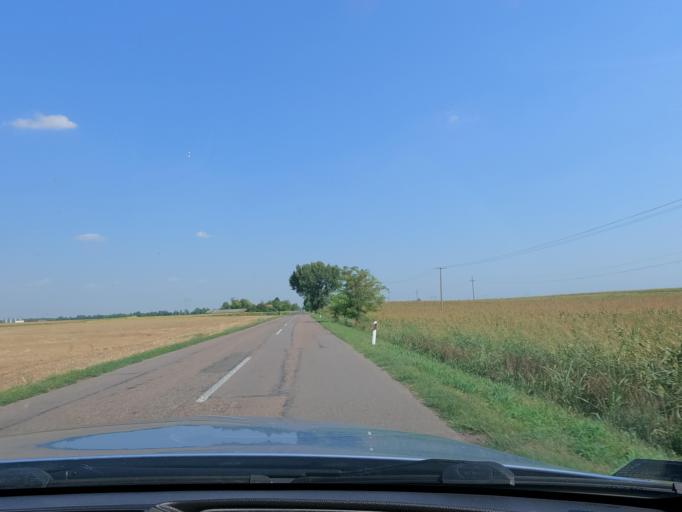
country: RS
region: Autonomna Pokrajina Vojvodina
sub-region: Severnobacki Okrug
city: Mali Igos
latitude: 45.7526
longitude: 19.7854
